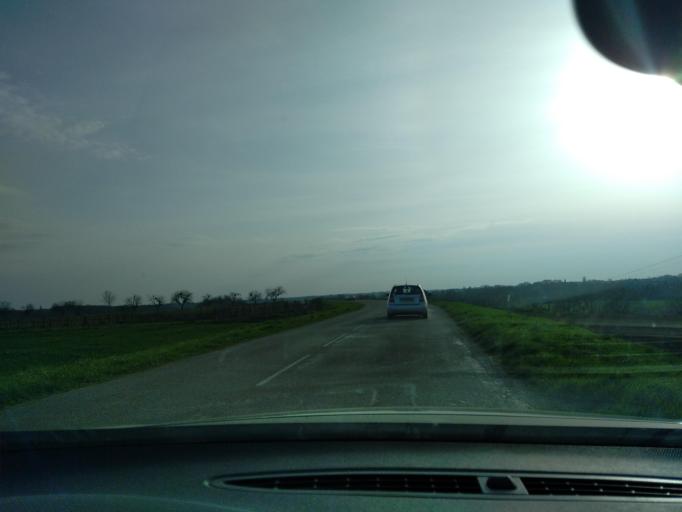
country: FR
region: Franche-Comte
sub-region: Departement du Jura
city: Chaussin
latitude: 46.9740
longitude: 5.4256
